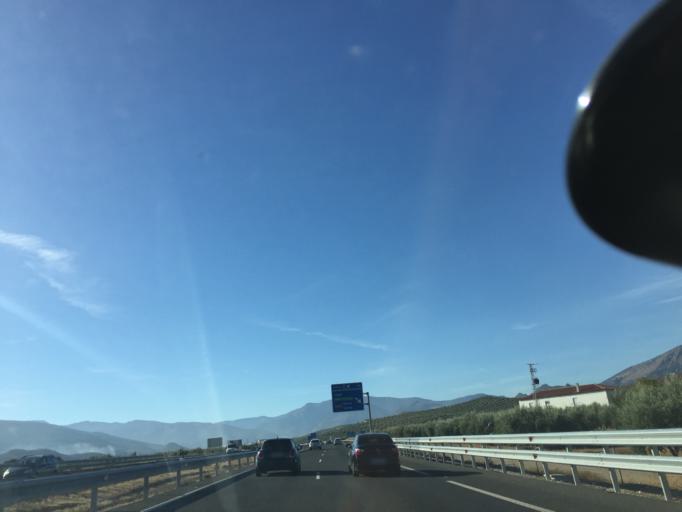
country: ES
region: Andalusia
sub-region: Provincia de Jaen
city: Jaen
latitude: 37.7976
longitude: -3.7580
